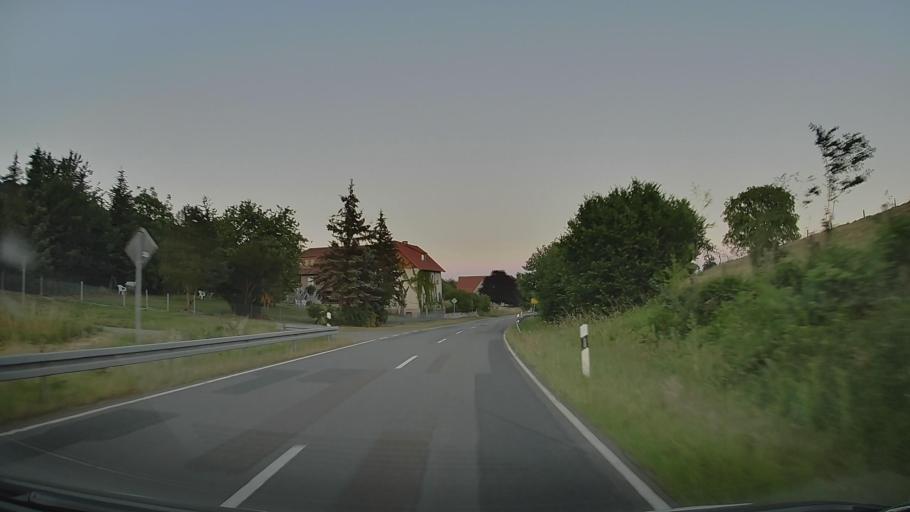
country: DE
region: Lower Saxony
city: Aerzen
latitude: 52.0198
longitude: 9.3027
